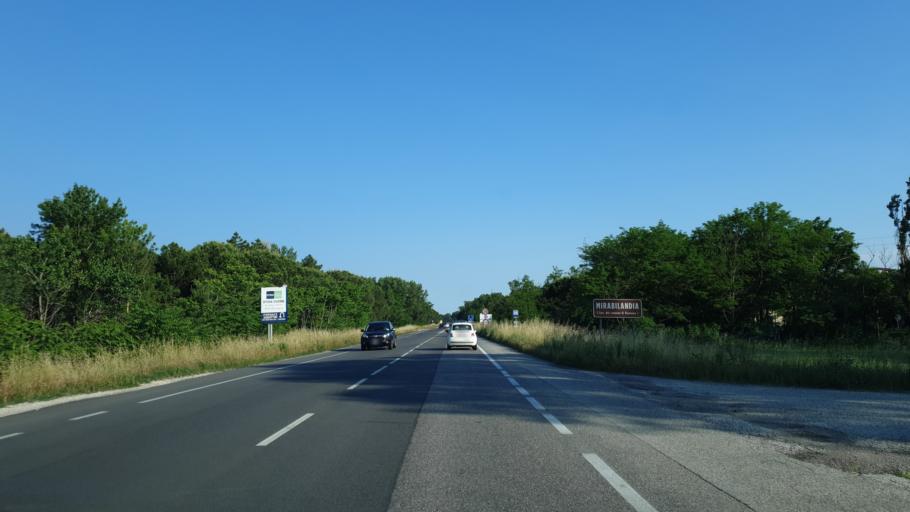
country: IT
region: Emilia-Romagna
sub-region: Provincia di Ravenna
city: Fosso Ghiaia
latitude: 44.3427
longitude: 12.2650
